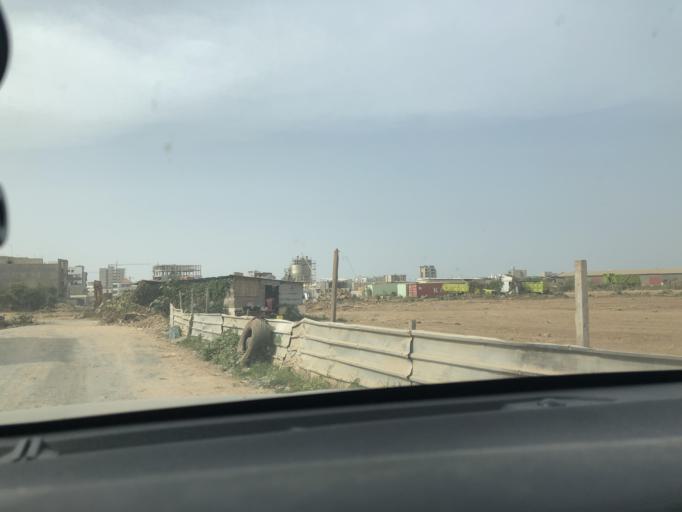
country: SN
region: Dakar
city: Mermoz Boabab
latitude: 14.7338
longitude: -17.4990
